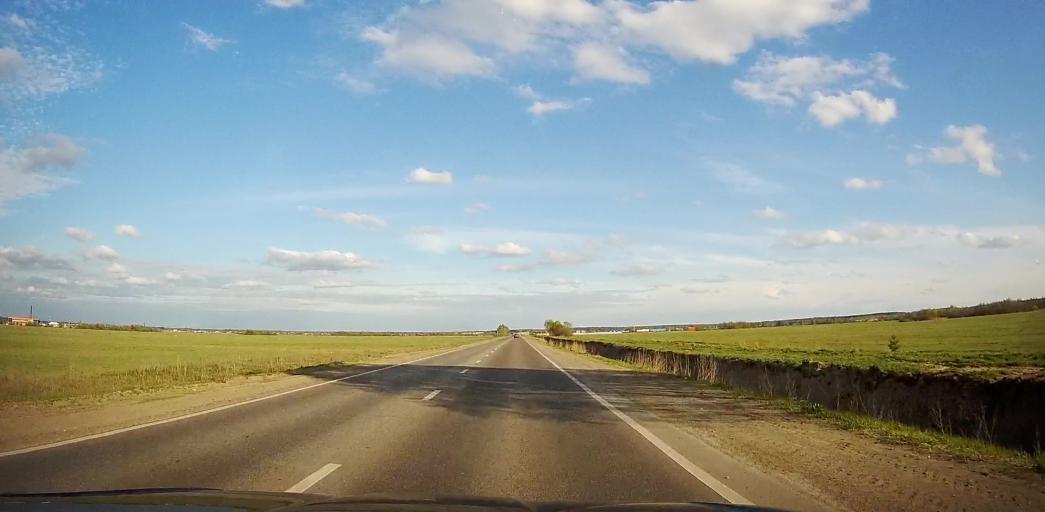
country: RU
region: Moskovskaya
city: Malyshevo
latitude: 55.5031
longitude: 38.2953
